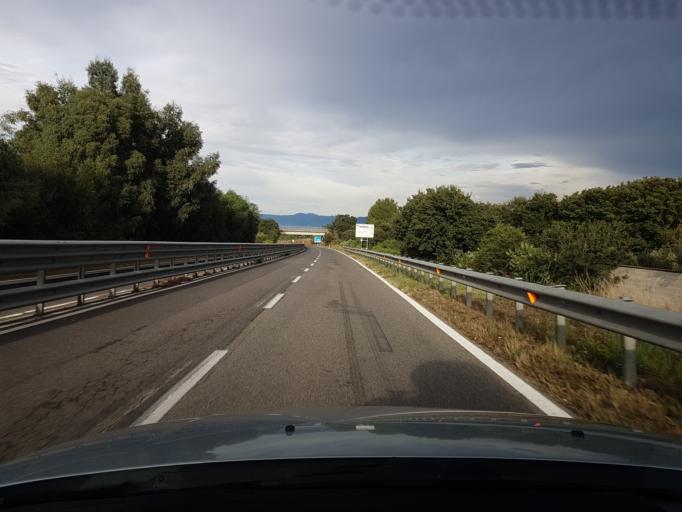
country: IT
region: Sardinia
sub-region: Provincia di Oristano
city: Ghilarza
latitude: 40.1159
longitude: 8.8361
